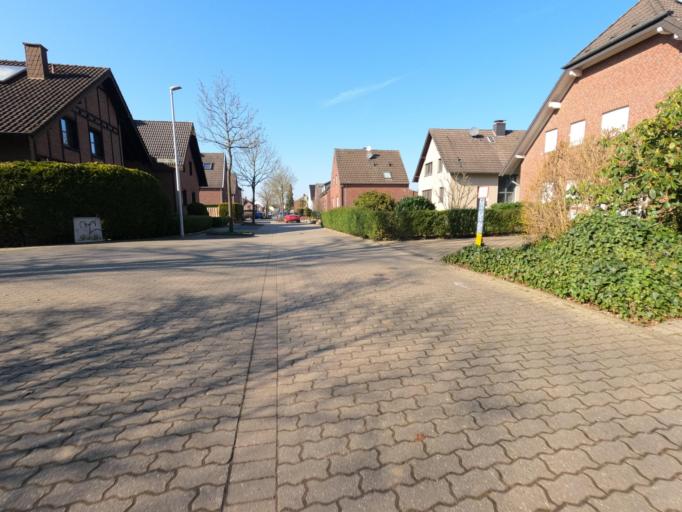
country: DE
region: North Rhine-Westphalia
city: Erkelenz
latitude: 51.0502
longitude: 6.2994
